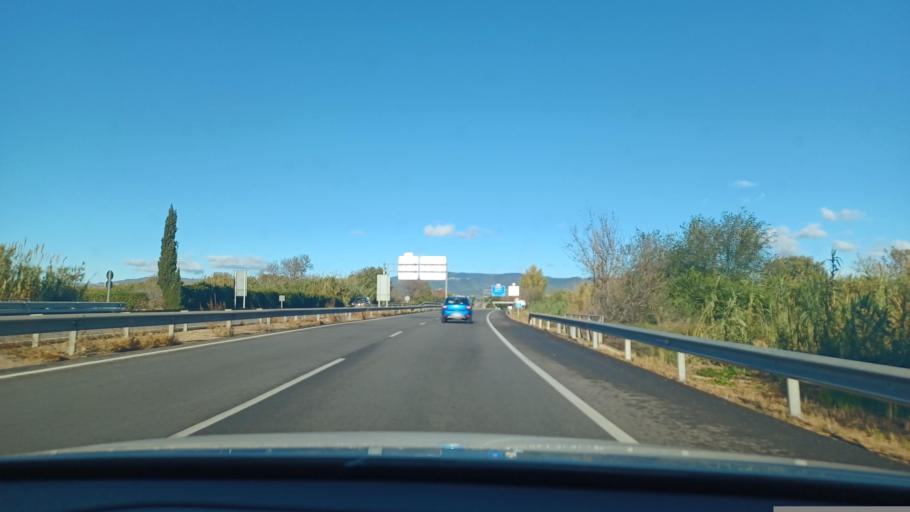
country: ES
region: Catalonia
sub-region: Provincia de Tarragona
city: Vila-seca
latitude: 41.1399
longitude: 1.1434
